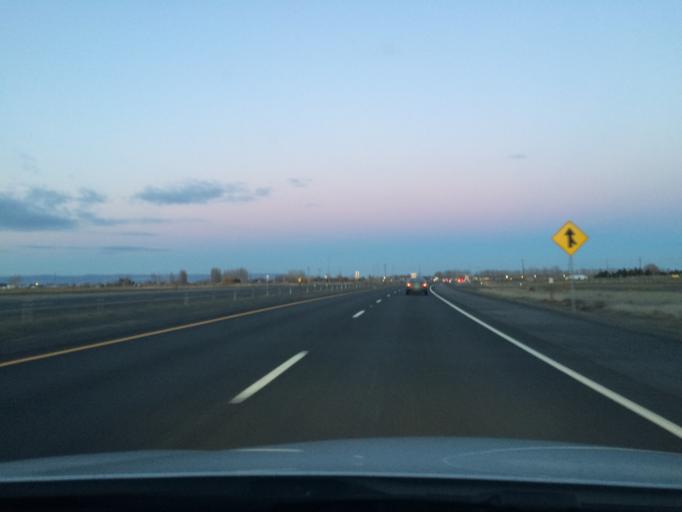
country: US
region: Washington
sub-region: Grant County
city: Quincy
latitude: 47.0850
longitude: -119.8612
